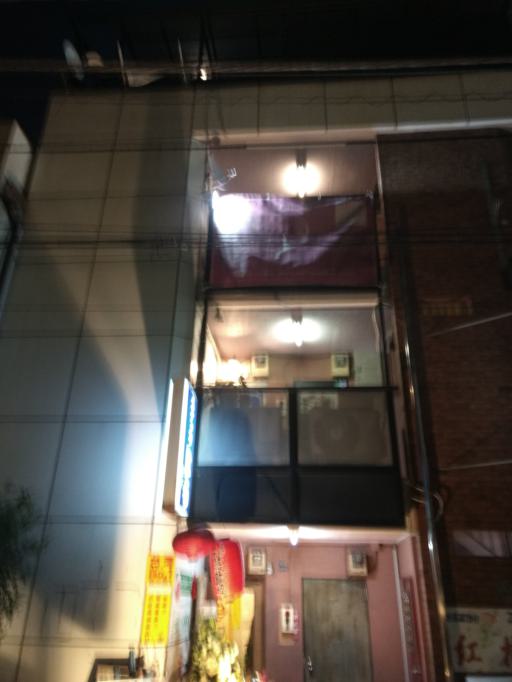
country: JP
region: Tokyo
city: Tokyo
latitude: 35.6943
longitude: 139.6956
